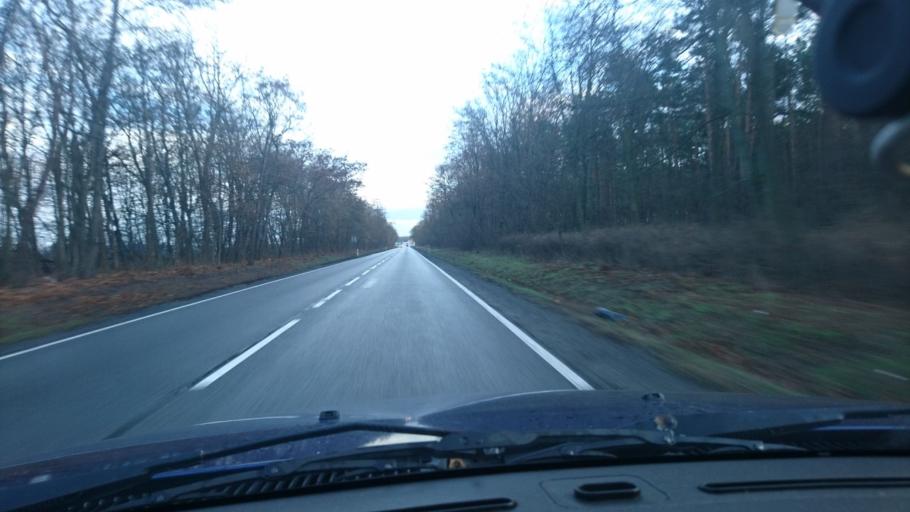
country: PL
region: Greater Poland Voivodeship
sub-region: Powiat kepinski
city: Kepno
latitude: 51.3234
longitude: 17.9688
